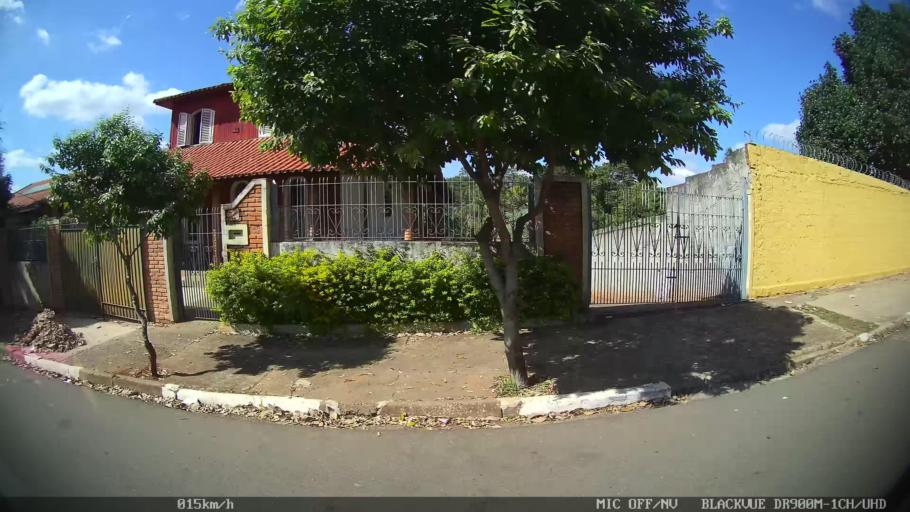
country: BR
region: Sao Paulo
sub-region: Hortolandia
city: Hortolandia
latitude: -22.8798
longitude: -47.2226
